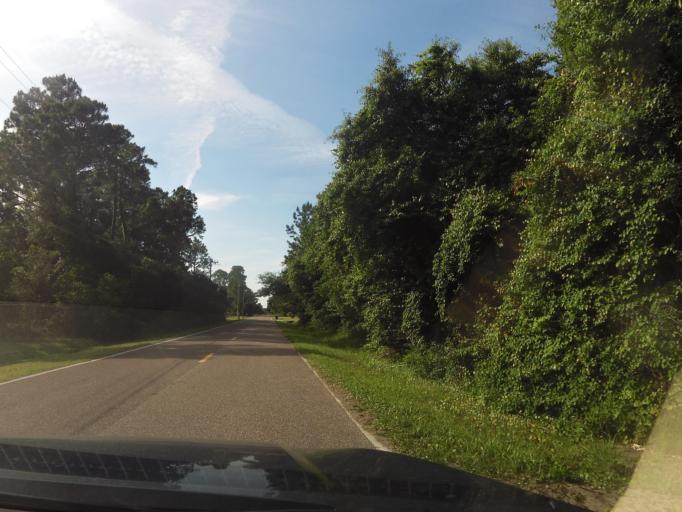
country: US
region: Florida
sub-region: Nassau County
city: Fernandina Beach
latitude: 30.5201
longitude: -81.4803
